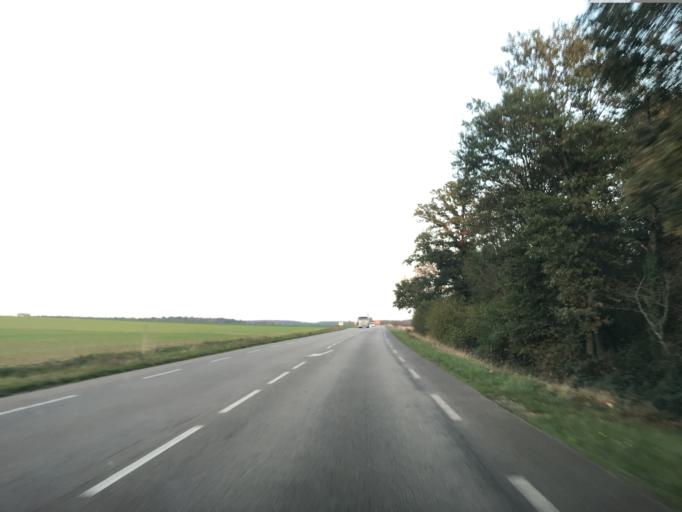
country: FR
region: Haute-Normandie
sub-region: Departement de l'Eure
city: Bourth
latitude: 48.7025
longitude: 0.8361
